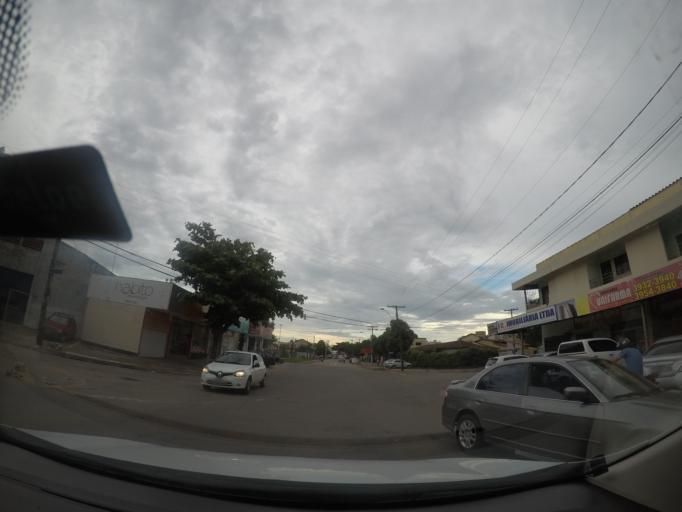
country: BR
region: Goias
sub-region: Goiania
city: Goiania
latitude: -16.6572
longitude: -49.2450
